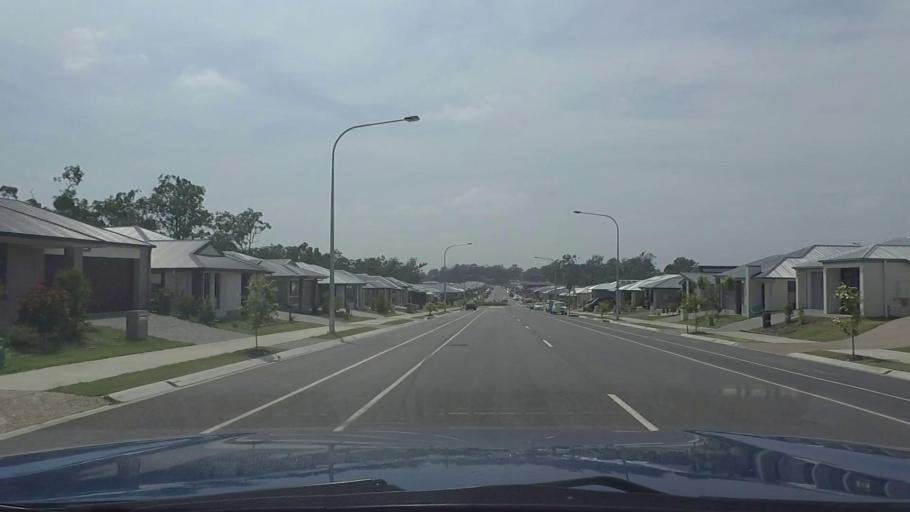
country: AU
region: Queensland
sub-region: Logan
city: Logan Reserve
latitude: -27.7039
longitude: 153.0994
